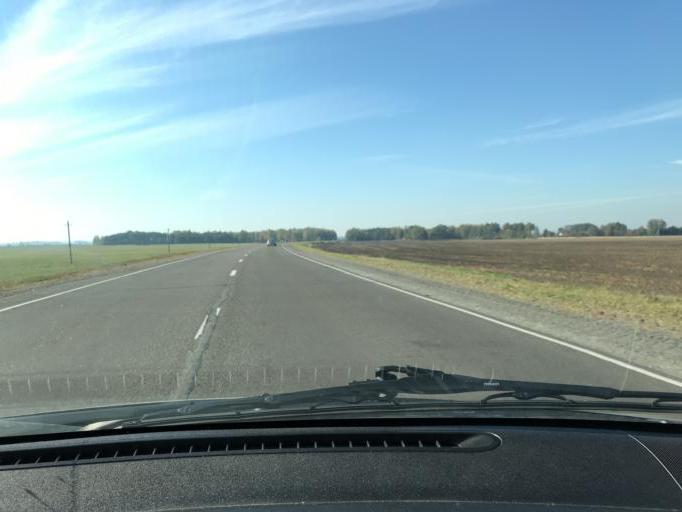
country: BY
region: Brest
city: Asnyezhytsy
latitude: 52.2766
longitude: 26.3948
